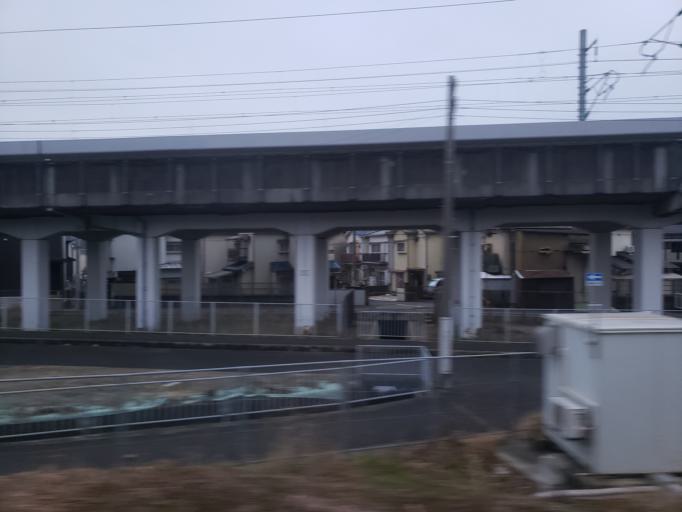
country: JP
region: Hyogo
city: Akashi
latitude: 34.6926
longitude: 134.9100
